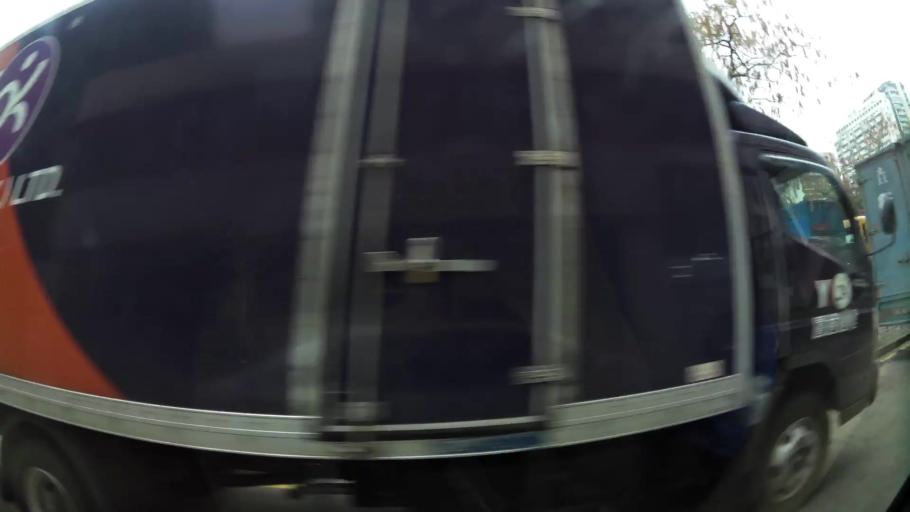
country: HK
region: Tsuen Wan
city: Tsuen Wan
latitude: 22.3575
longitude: 114.1217
